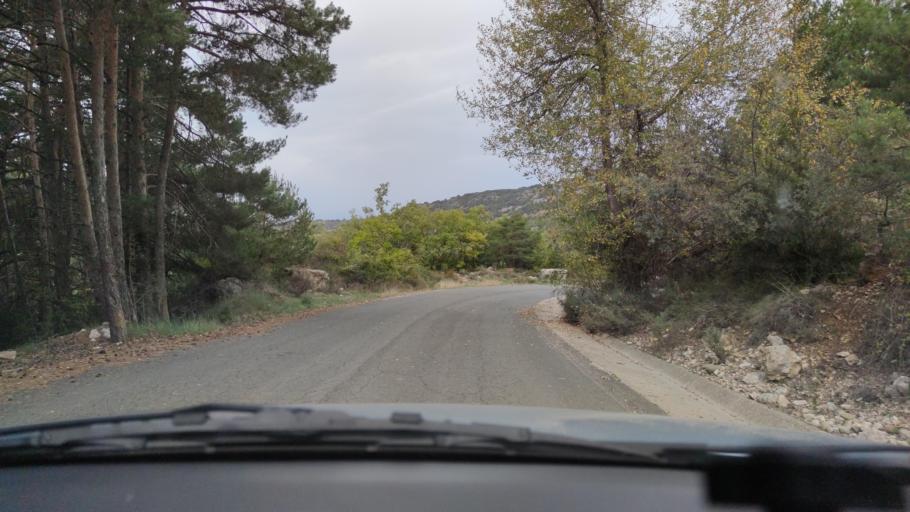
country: ES
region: Catalonia
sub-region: Provincia de Lleida
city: Llimiana
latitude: 42.0440
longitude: 1.0010
